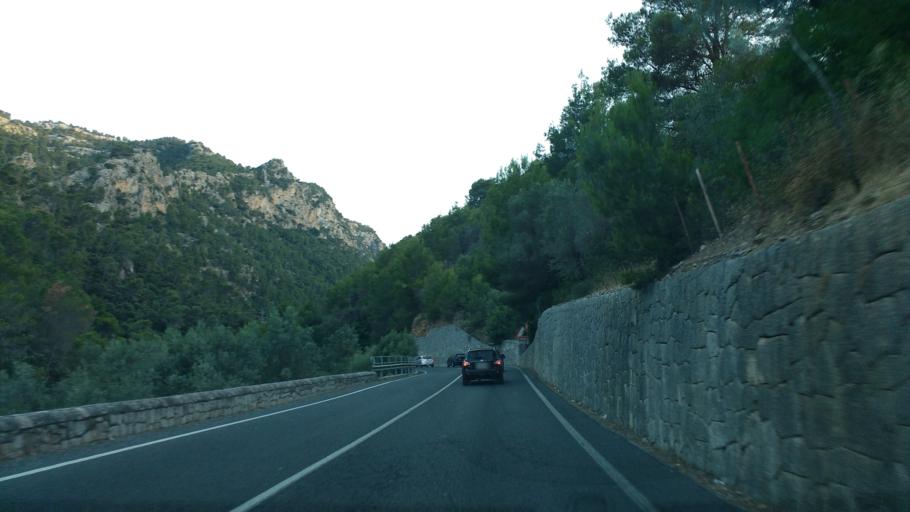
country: ES
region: Balearic Islands
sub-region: Illes Balears
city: Soller
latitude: 39.7552
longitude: 2.7075
